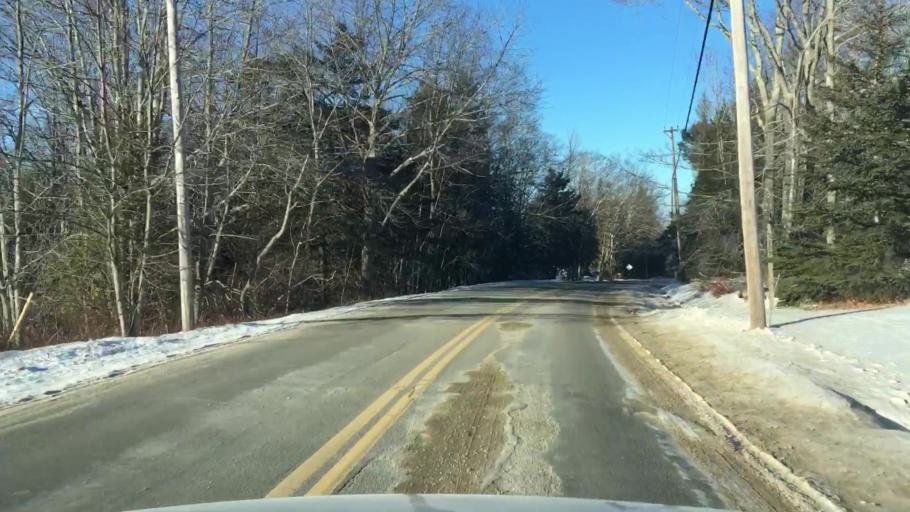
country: US
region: Maine
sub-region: Hancock County
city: Castine
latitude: 44.3760
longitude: -68.7522
